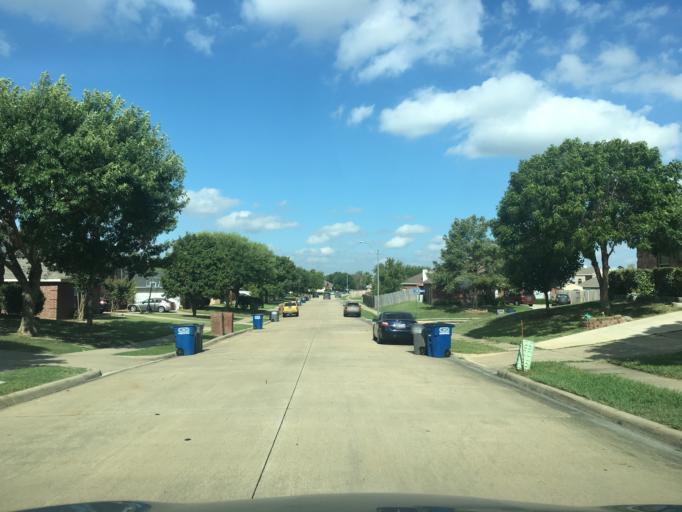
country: US
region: Texas
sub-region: Dallas County
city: Sachse
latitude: 32.9549
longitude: -96.5881
